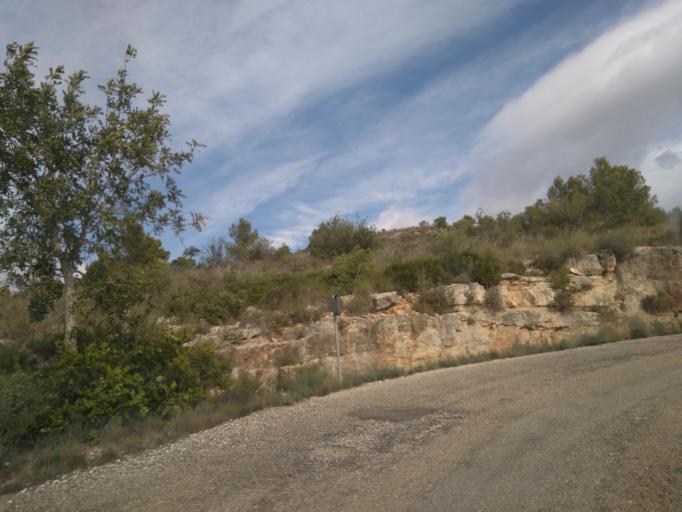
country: ES
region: Valencia
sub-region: Provincia de Valencia
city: Sumacarcer
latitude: 39.1479
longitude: -0.6433
